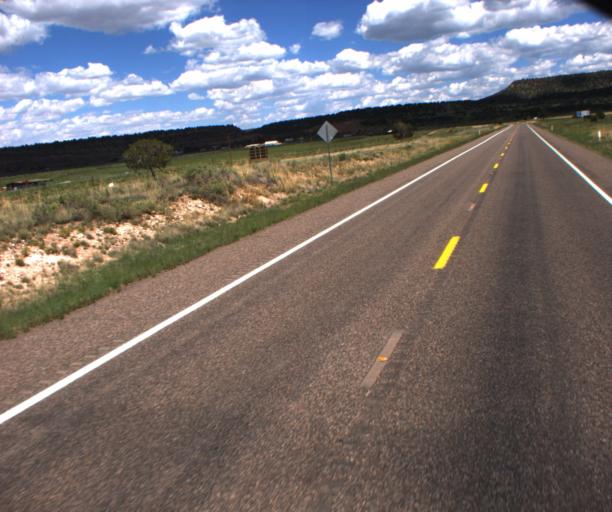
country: US
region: Arizona
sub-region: Apache County
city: Springerville
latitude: 34.1324
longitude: -109.2480
